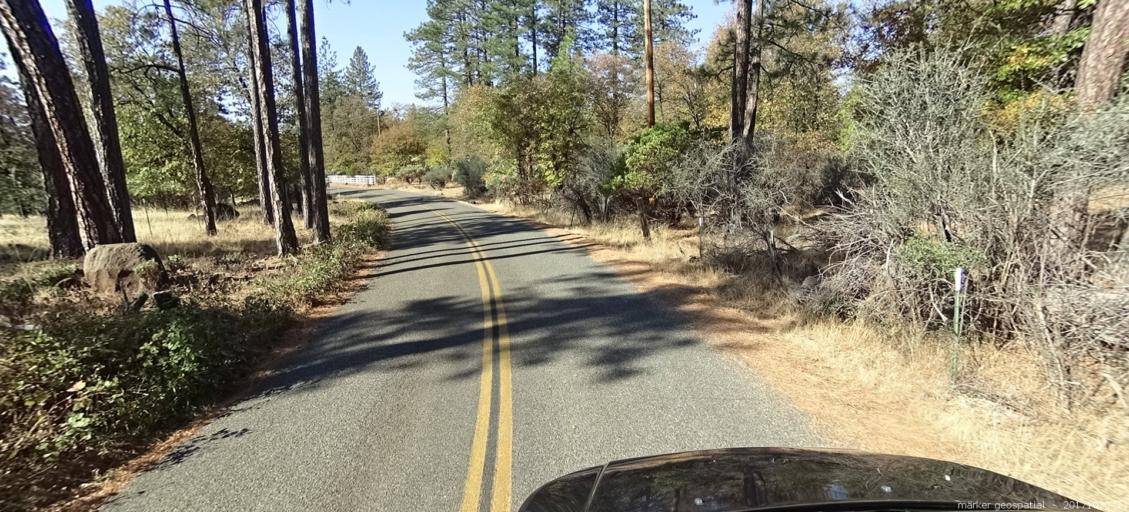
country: US
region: California
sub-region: Shasta County
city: Shingletown
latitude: 40.6008
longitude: -121.9689
